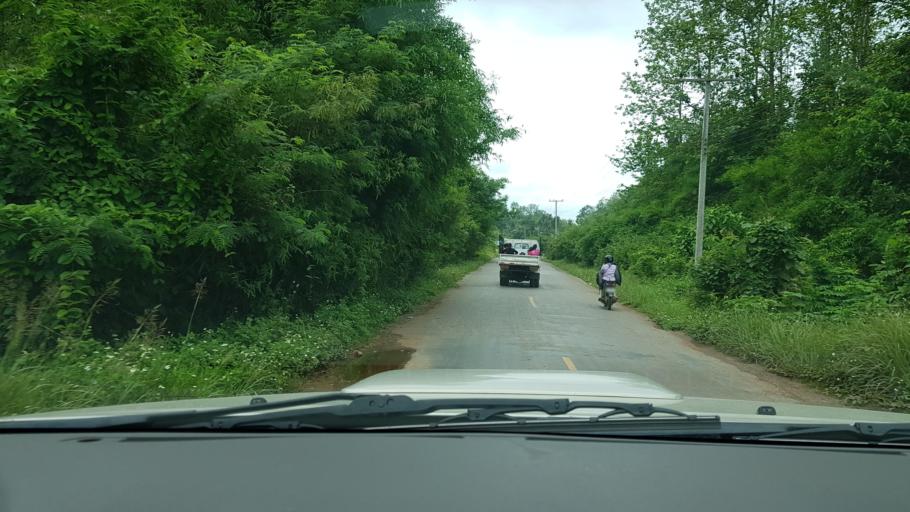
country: LA
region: Loungnamtha
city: Muang Nale
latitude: 20.3136
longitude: 101.6533
